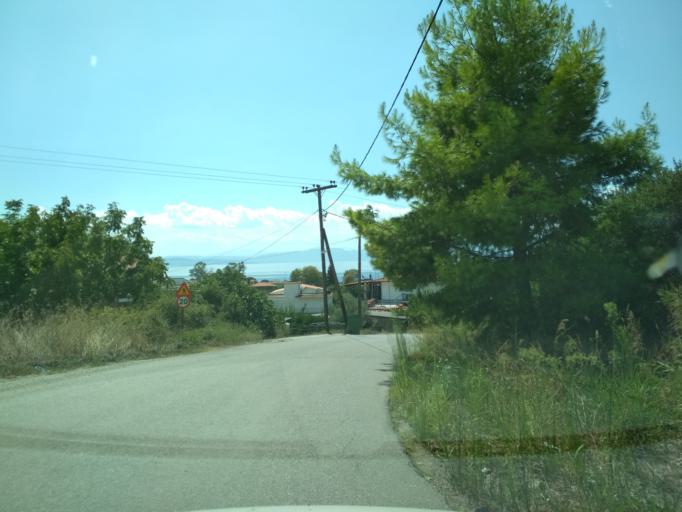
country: GR
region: Central Greece
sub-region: Nomos Evvoias
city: Roviai
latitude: 38.8143
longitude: 23.2299
